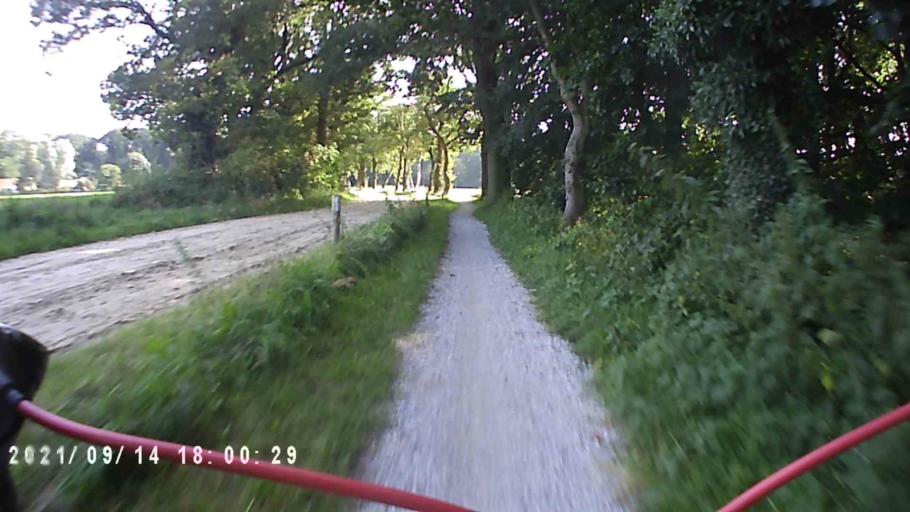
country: NL
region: Drenthe
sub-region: Gemeente Tynaarlo
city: Zuidlaren
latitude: 53.1212
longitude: 6.6496
